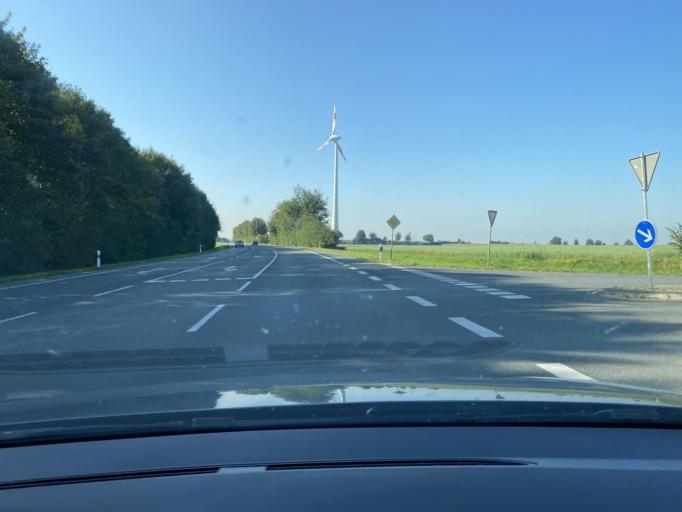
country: DE
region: North Rhine-Westphalia
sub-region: Regierungsbezirk Munster
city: Schoppingen
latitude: 52.0901
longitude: 7.2688
